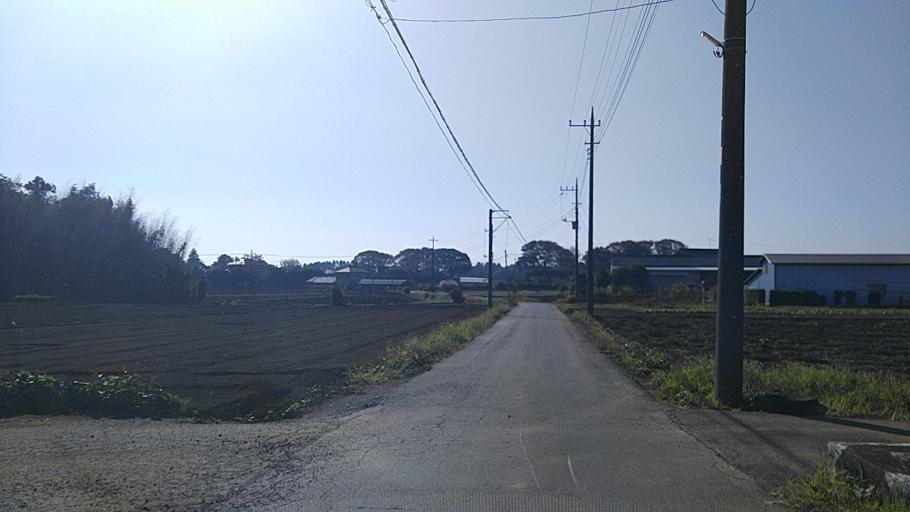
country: JP
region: Chiba
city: Sawara
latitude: 35.8389
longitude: 140.4681
